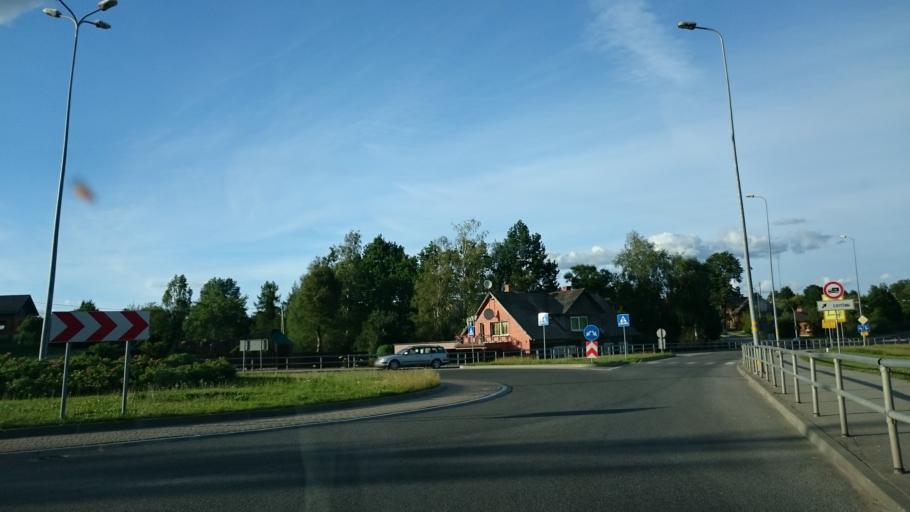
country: LV
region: Saldus Rajons
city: Saldus
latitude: 56.6632
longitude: 22.4773
